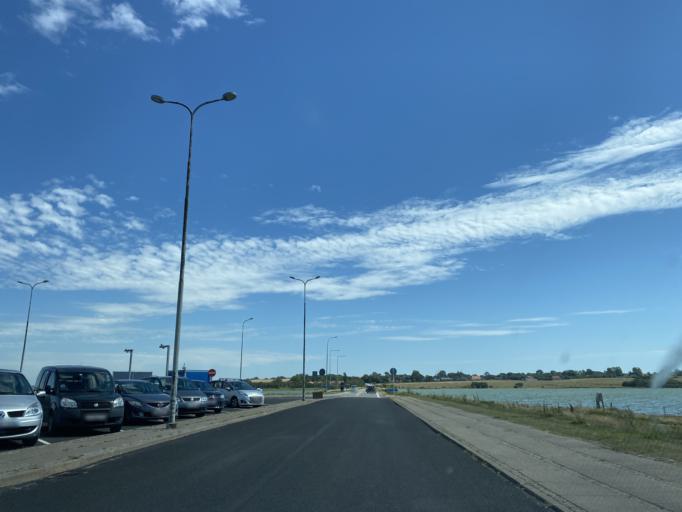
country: DK
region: South Denmark
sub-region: Assens Kommune
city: Harby
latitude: 55.1043
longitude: 10.0836
